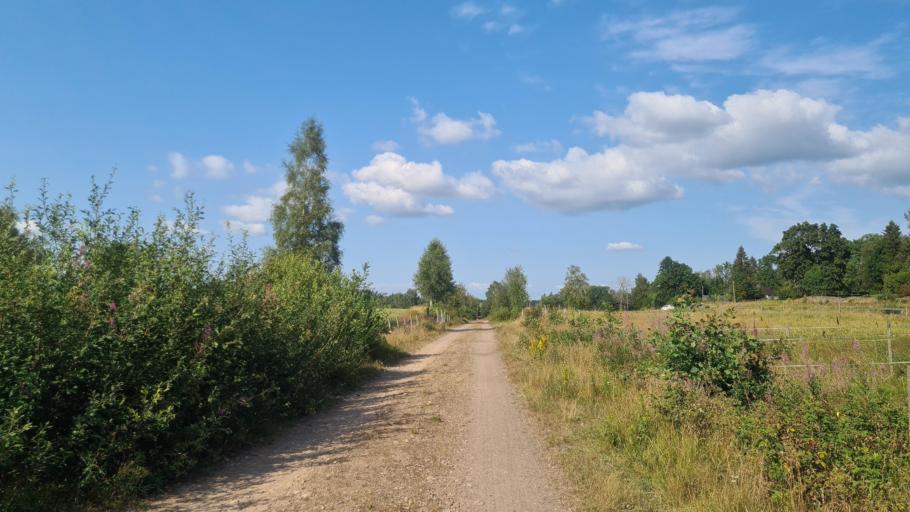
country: SE
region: Kronoberg
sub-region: Ljungby Kommun
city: Ljungby
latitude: 56.7742
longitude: 13.9006
